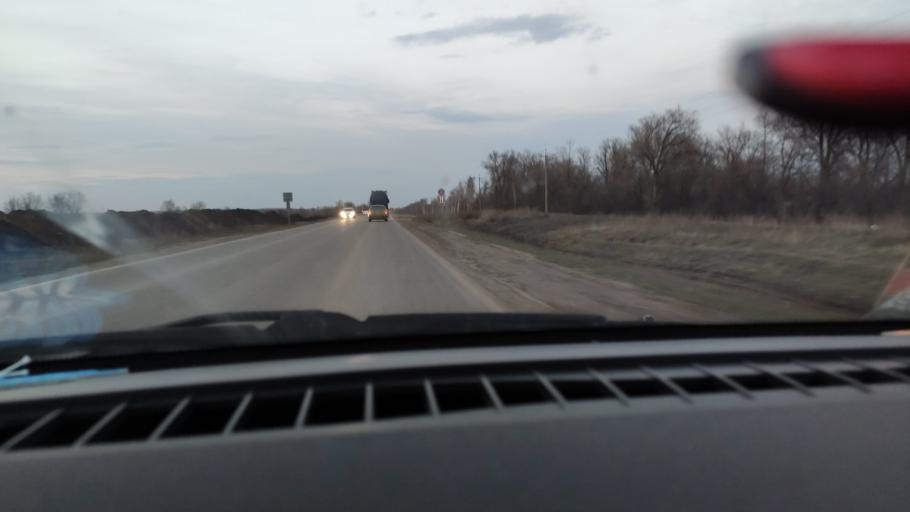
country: RU
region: Saratov
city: Sinodskoye
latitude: 52.0181
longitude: 46.7016
